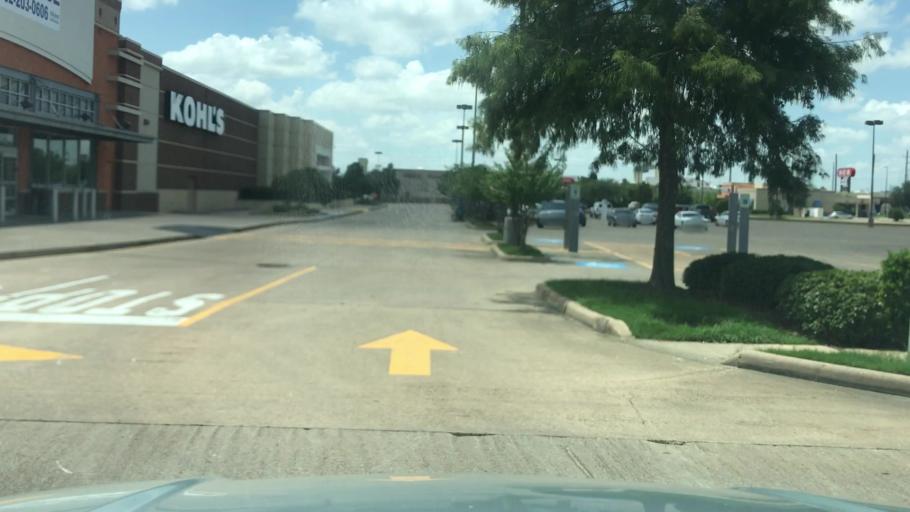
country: US
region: Texas
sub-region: Fort Bend County
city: Cinco Ranch
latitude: 29.7880
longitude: -95.7173
